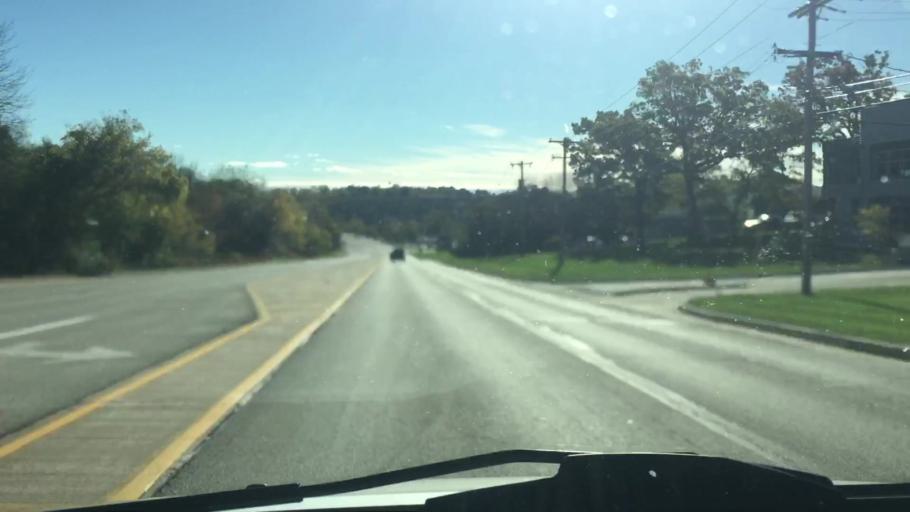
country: US
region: Wisconsin
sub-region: Waukesha County
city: Waukesha
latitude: 43.0395
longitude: -88.2197
